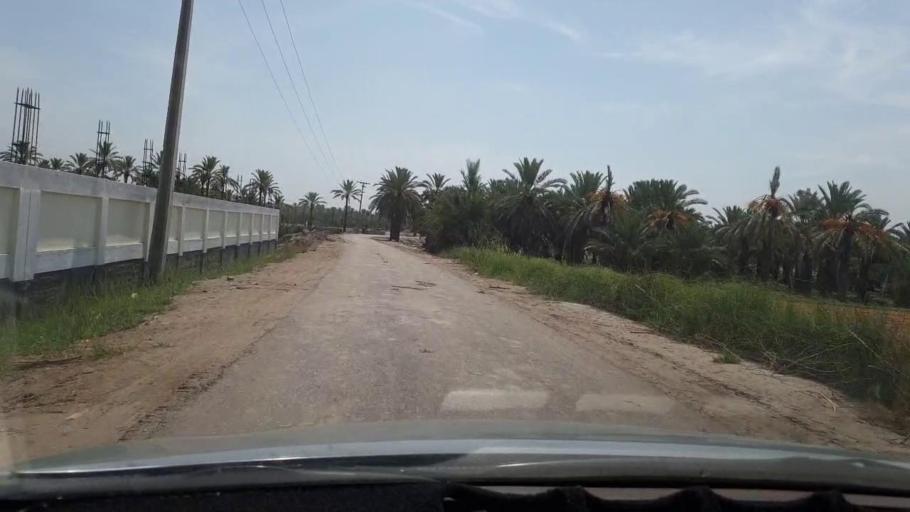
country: PK
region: Sindh
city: Khairpur
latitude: 27.4881
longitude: 68.7607
